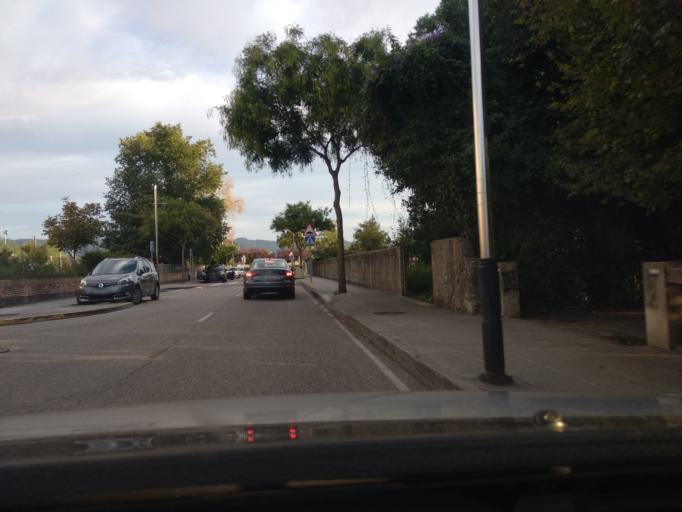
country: ES
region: Galicia
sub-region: Provincia de Pontevedra
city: Moana
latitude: 42.2884
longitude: -8.7312
